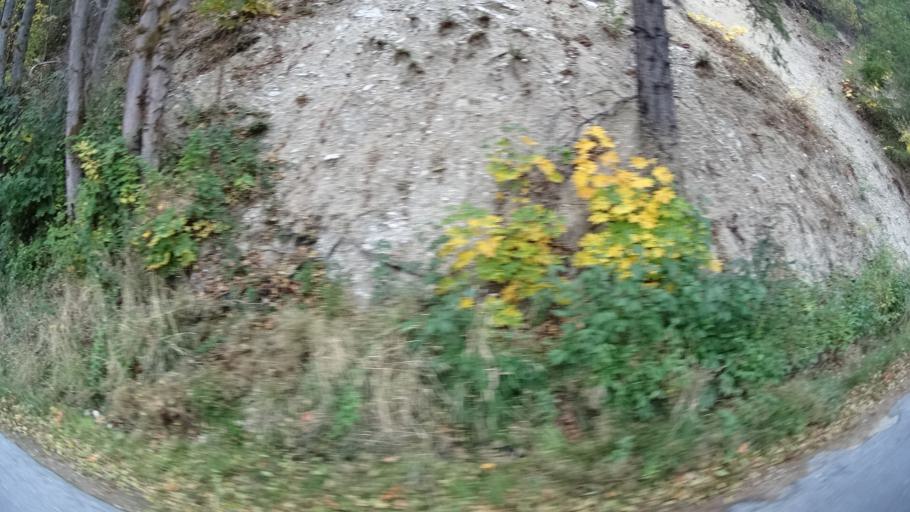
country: US
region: California
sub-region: Siskiyou County
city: Happy Camp
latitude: 41.8285
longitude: -123.1931
